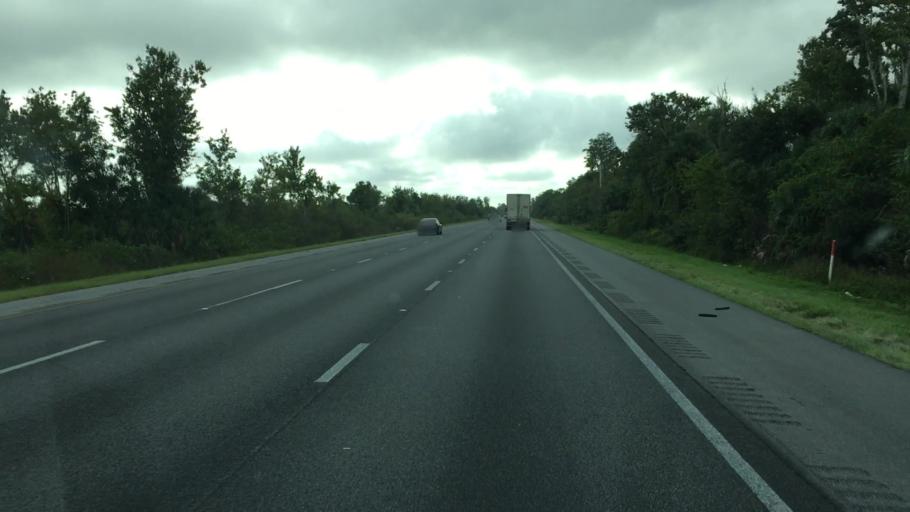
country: US
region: Florida
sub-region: Volusia County
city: Glencoe
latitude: 29.0359
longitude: -81.0034
